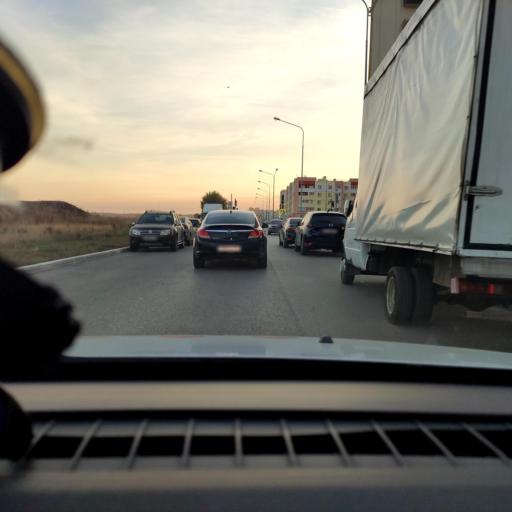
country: RU
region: Samara
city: Samara
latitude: 53.1152
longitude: 50.1464
